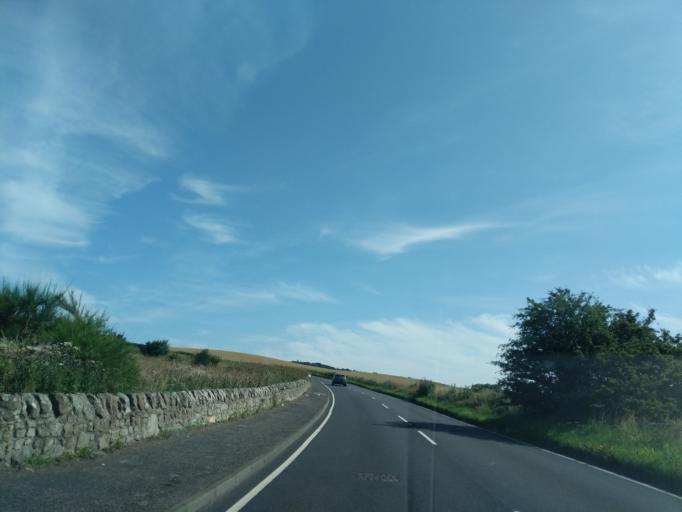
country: GB
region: Scotland
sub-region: Fife
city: Saint Andrews
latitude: 56.3319
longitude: -2.7822
